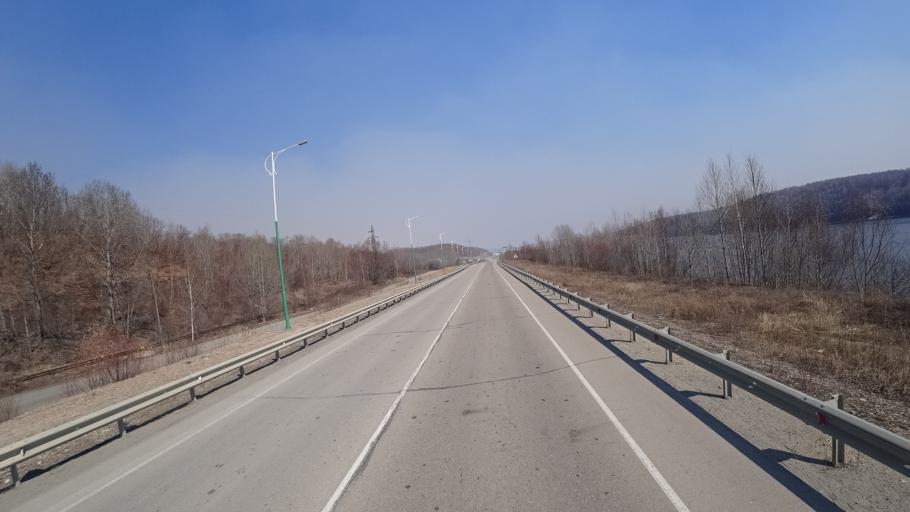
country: RU
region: Amur
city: Novobureyskiy
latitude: 49.7877
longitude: 129.9548
